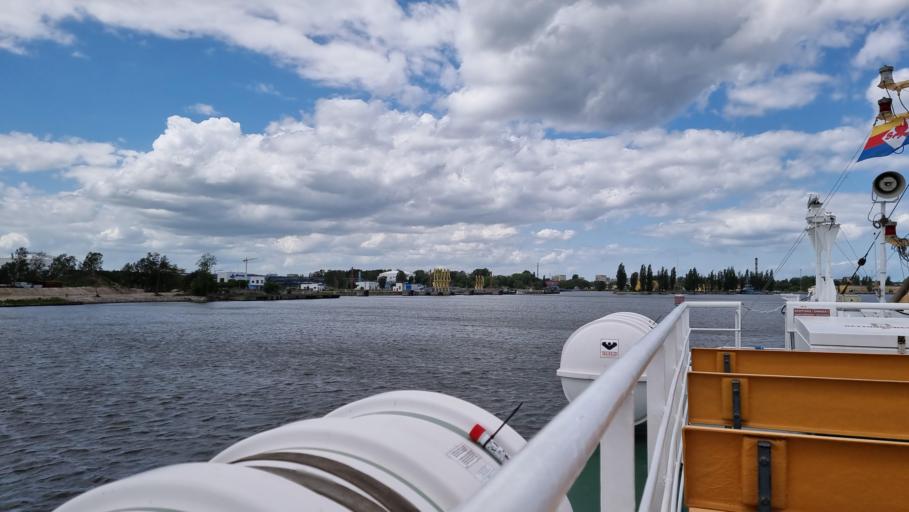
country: PL
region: West Pomeranian Voivodeship
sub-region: Swinoujscie
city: Swinoujscie
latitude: 53.8918
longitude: 14.2566
